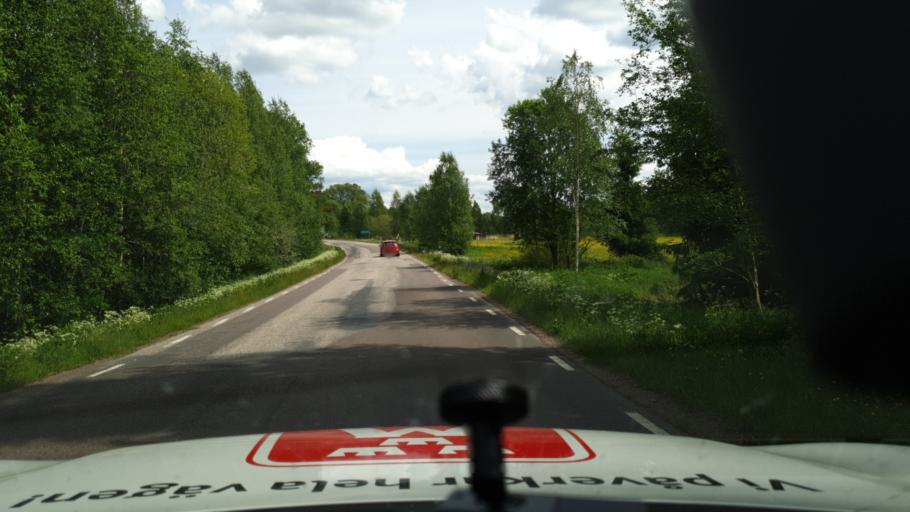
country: SE
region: Vaermland
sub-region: Torsby Kommun
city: Torsby
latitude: 59.9882
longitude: 12.8506
